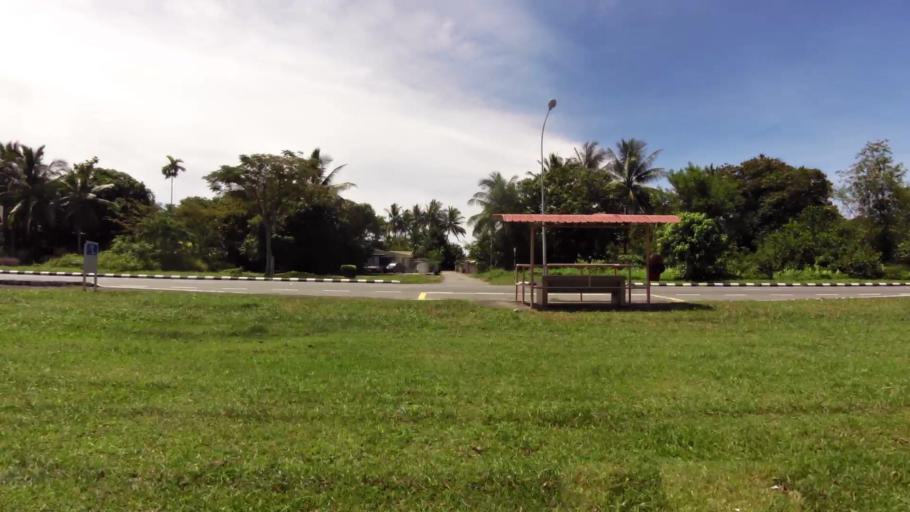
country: BN
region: Belait
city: Kuala Belait
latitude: 4.5915
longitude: 114.2227
